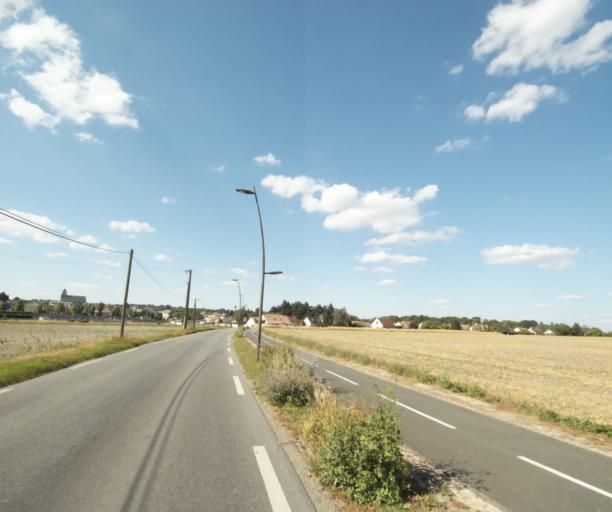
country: FR
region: Centre
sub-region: Departement du Loiret
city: Ingre
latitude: 47.9134
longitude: 1.8302
